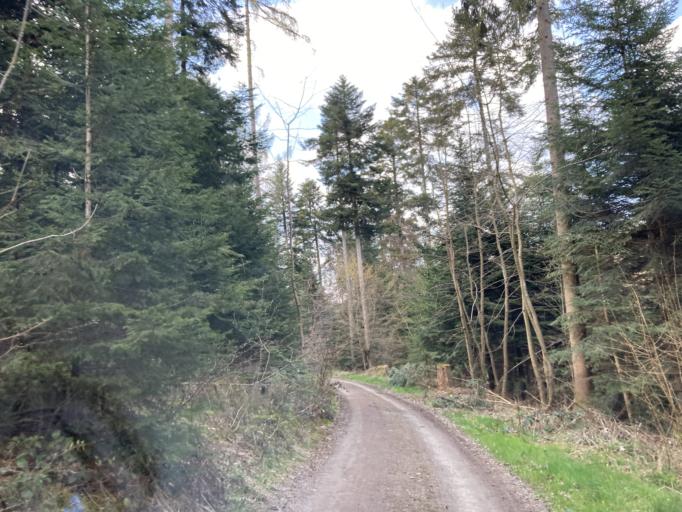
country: DE
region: Baden-Wuerttemberg
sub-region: Karlsruhe Region
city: Dobel
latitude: 48.8345
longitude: 8.5216
